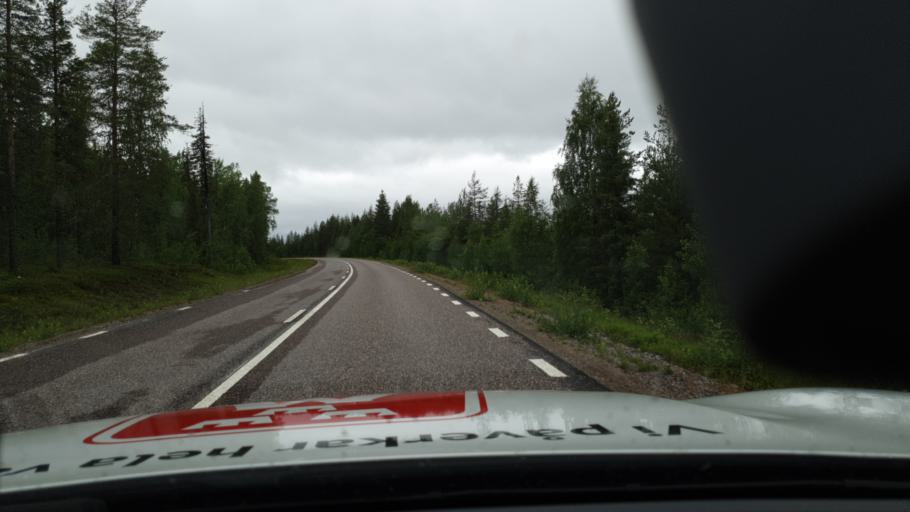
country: SE
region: Norrbotten
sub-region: Pajala Kommun
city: Pajala
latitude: 67.1614
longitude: 23.5429
